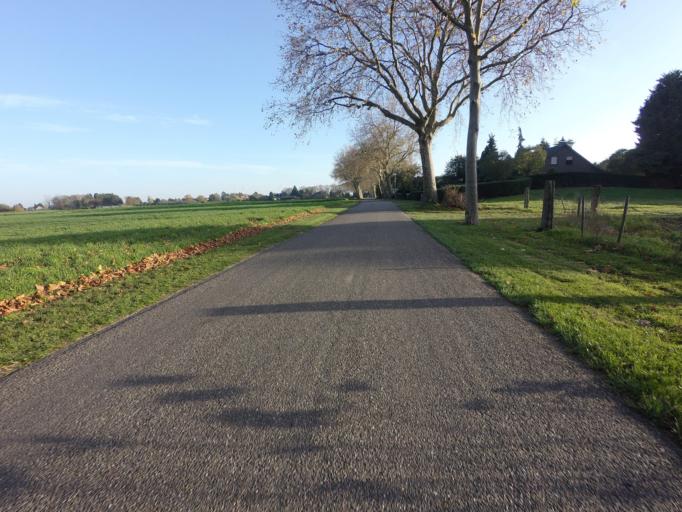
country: NL
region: Limburg
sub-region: Gemeente Echt-Susteren
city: Koningsbosch
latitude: 51.0595
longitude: 5.9413
